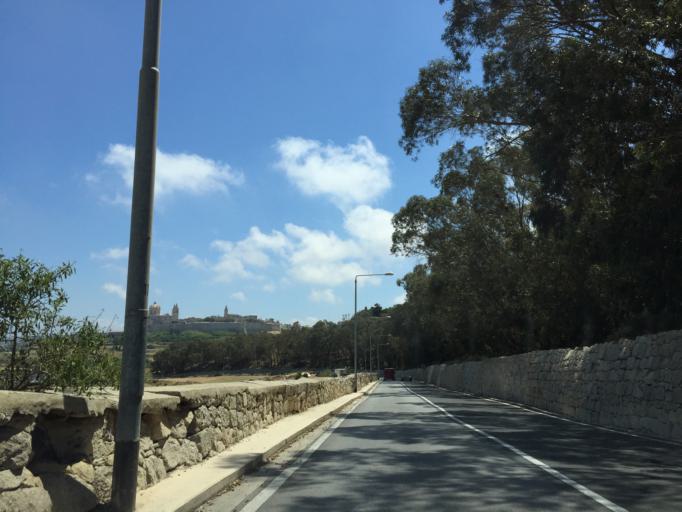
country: MT
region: L-Imtarfa
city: Imtarfa
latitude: 35.8953
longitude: 14.4036
